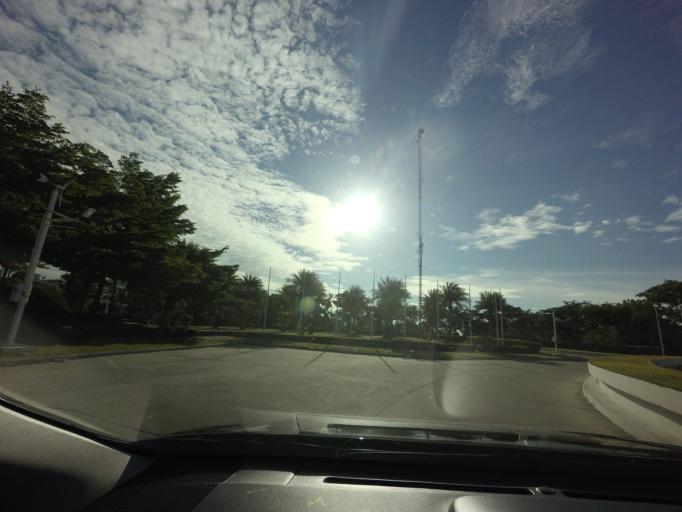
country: TH
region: Chon Buri
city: Bang Lamung
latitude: 13.1029
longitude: 100.9279
